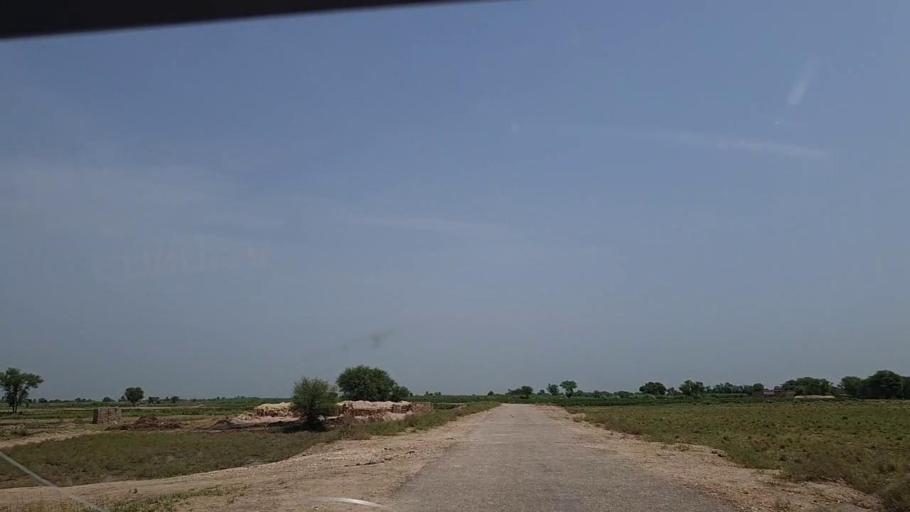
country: PK
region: Sindh
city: Tharu Shah
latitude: 26.9038
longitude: 68.0541
